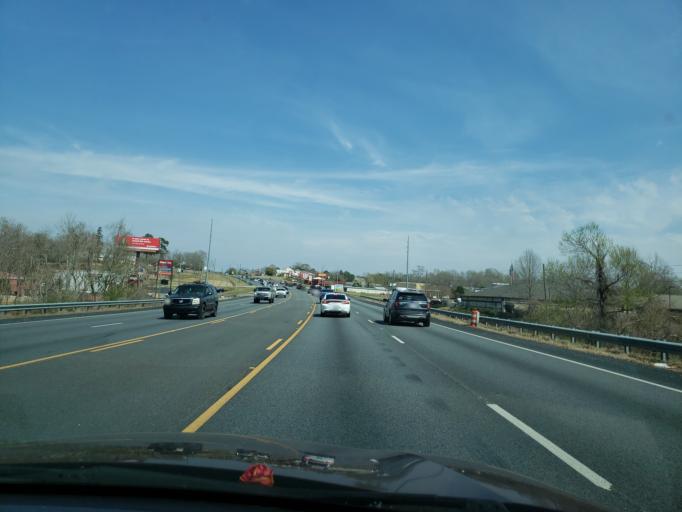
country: US
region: Alabama
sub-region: Elmore County
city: Millbrook
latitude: 32.5060
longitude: -86.3847
